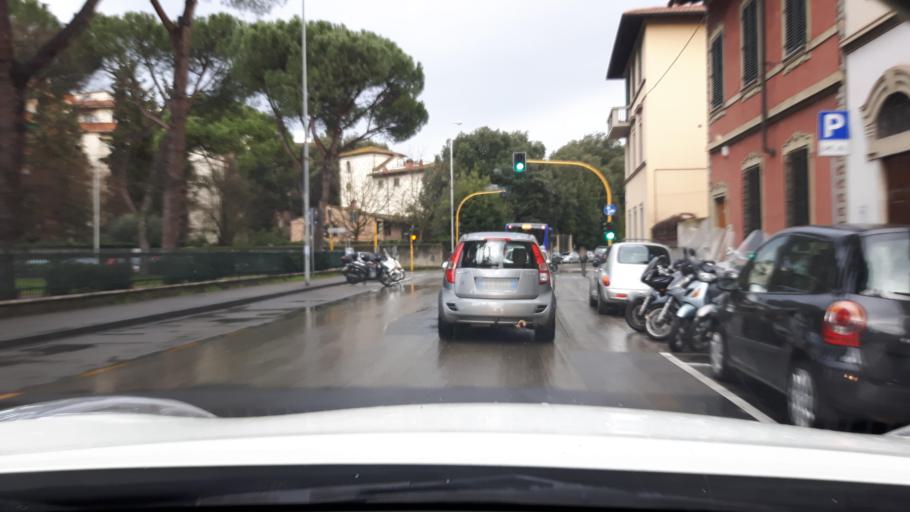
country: IT
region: Tuscany
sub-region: Province of Florence
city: Fiesole
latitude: 43.7765
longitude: 11.2935
